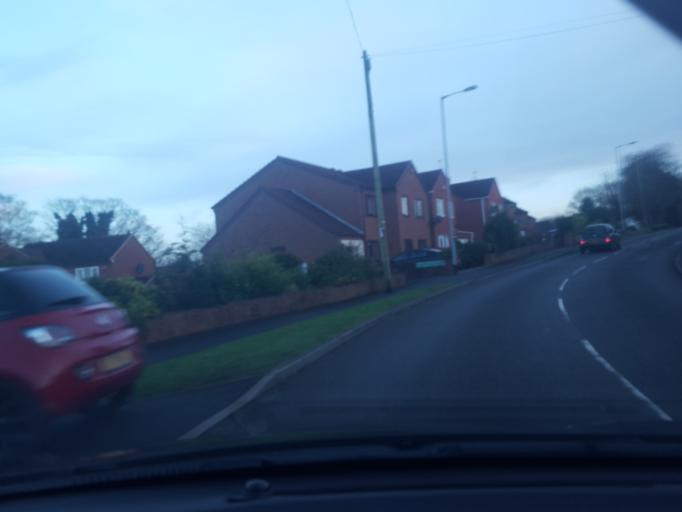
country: GB
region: England
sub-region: Staffordshire
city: Codsall
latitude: 52.6311
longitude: -2.1825
